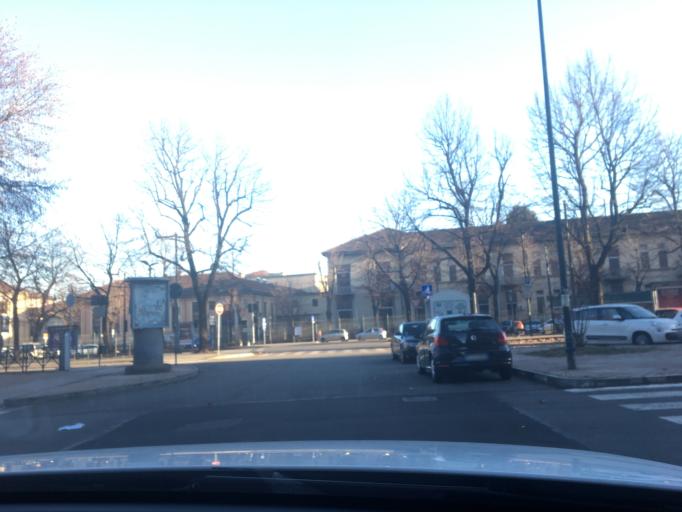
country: IT
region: Piedmont
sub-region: Provincia di Torino
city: Turin
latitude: 45.0522
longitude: 7.6634
